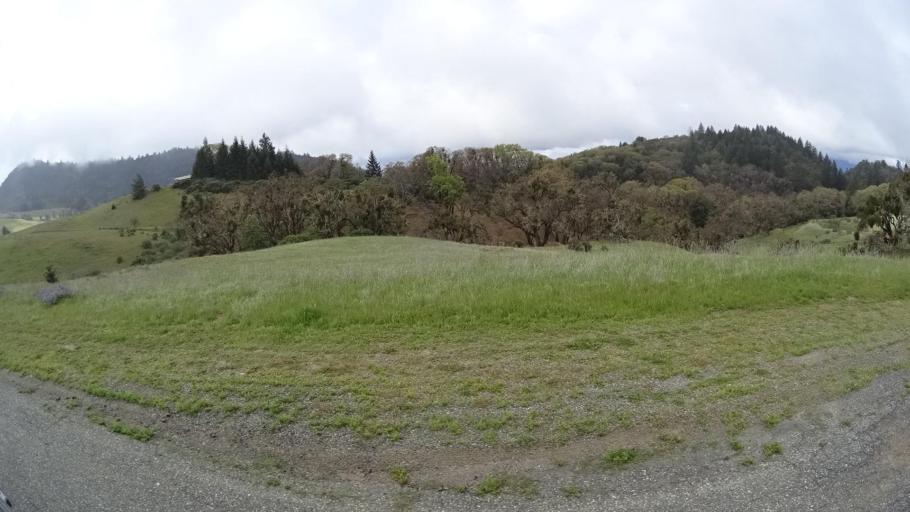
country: US
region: California
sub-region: Humboldt County
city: Redway
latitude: 40.1552
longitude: -123.5414
